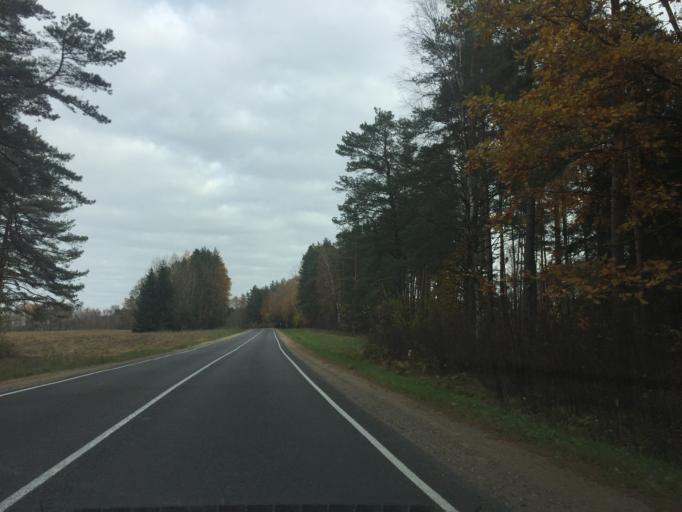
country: BY
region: Minsk
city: Svir
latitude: 54.8225
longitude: 26.1839
